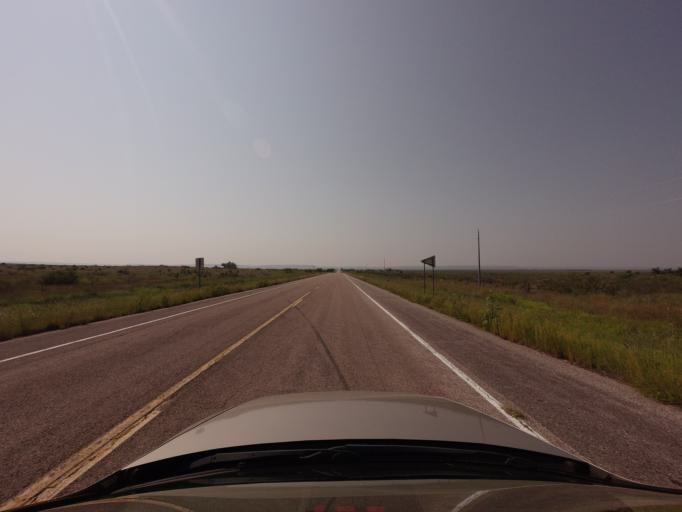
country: US
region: New Mexico
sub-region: Quay County
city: Tucumcari
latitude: 34.9427
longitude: -103.7602
